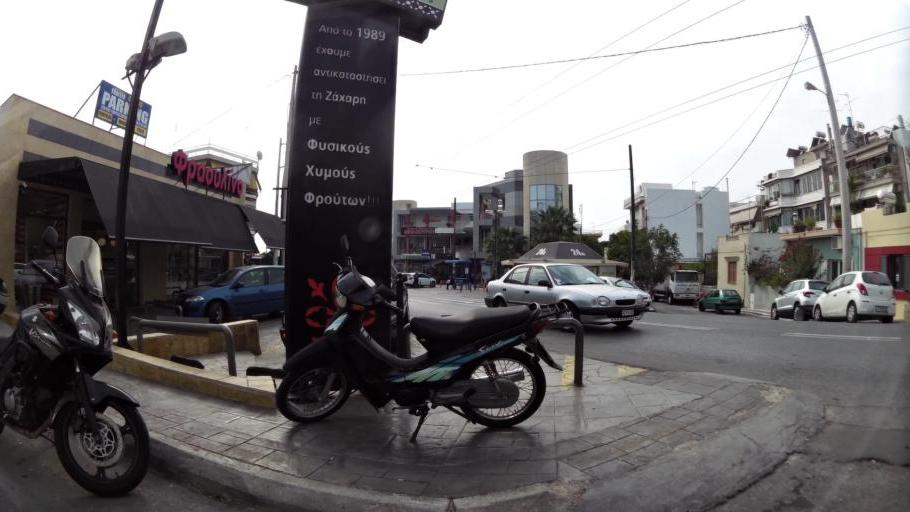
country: GR
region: Attica
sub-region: Nomarchia Athinas
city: Peristeri
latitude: 38.0258
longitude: 23.6825
